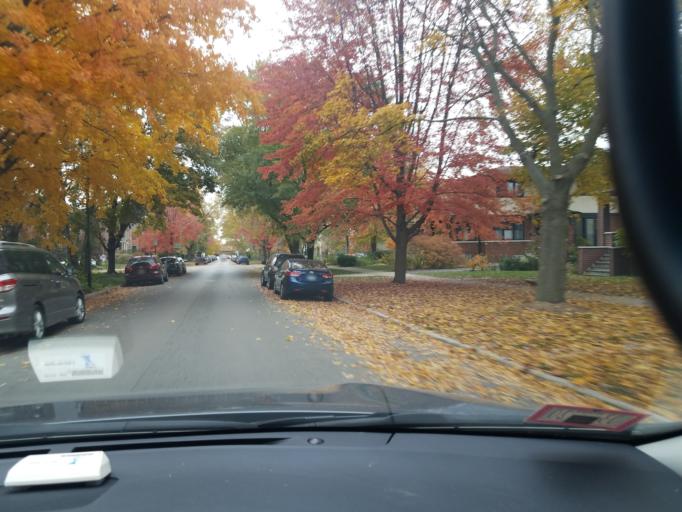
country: US
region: Illinois
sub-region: Cook County
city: Lincolnwood
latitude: 41.9511
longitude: -87.7324
